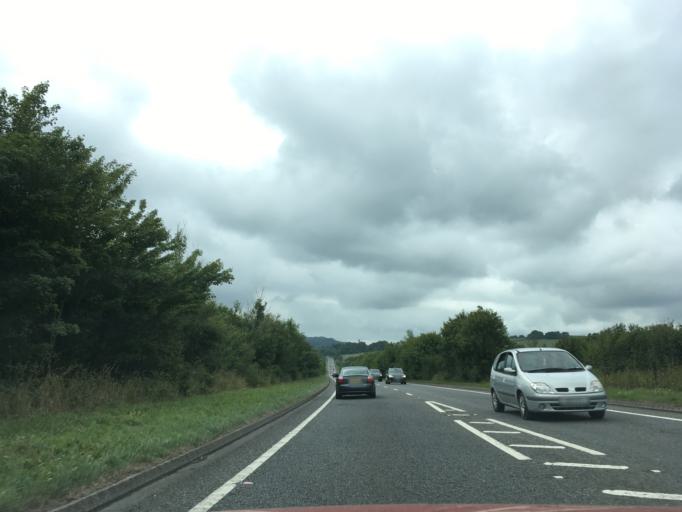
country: GB
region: Wales
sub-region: Carmarthenshire
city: Whitland
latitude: 51.8253
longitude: -4.5987
